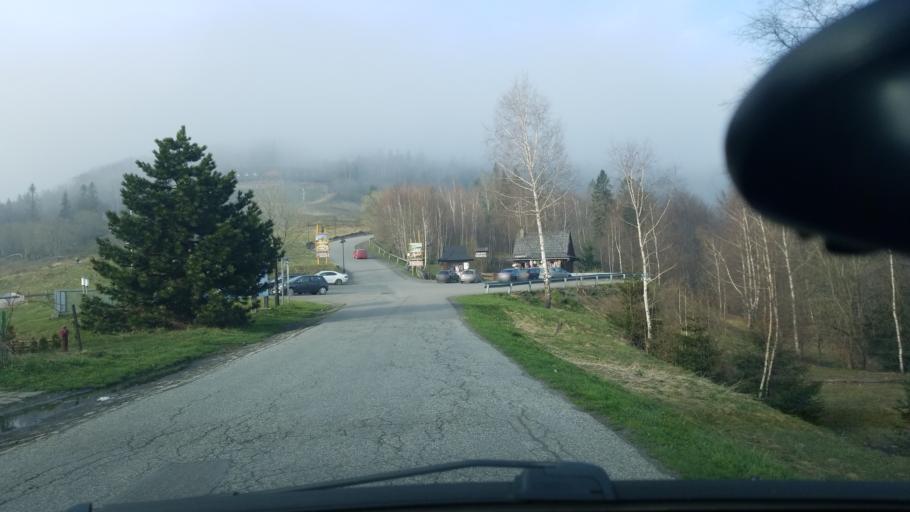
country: PL
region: Silesian Voivodeship
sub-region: Powiat cieszynski
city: Ustron
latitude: 49.7195
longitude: 18.8522
